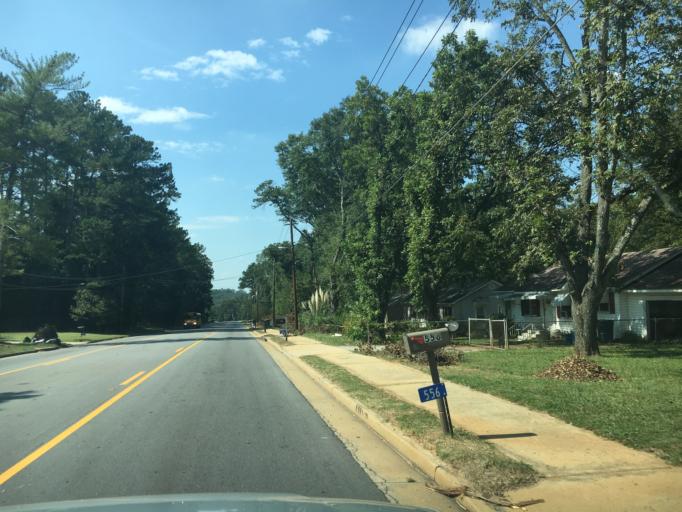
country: US
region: Georgia
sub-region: Hart County
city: Hartwell
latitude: 34.3585
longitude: -82.9462
